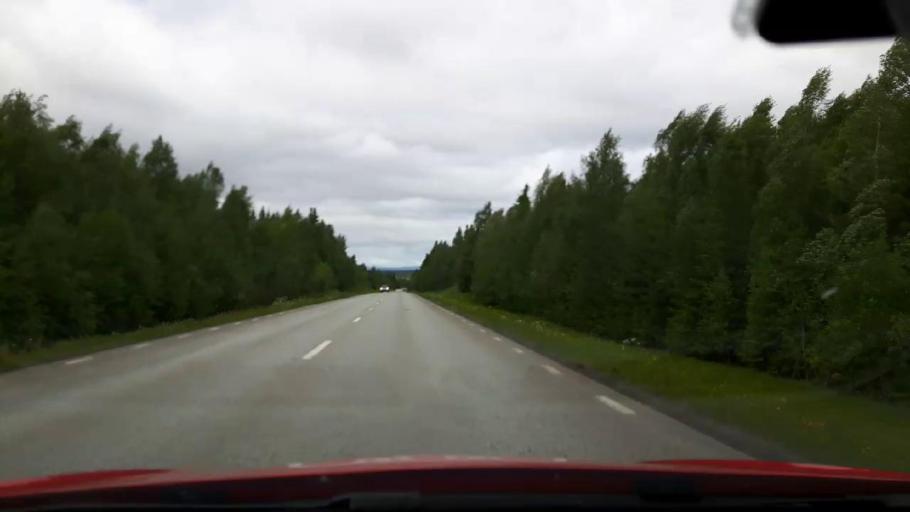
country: SE
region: Jaemtland
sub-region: Krokoms Kommun
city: Krokom
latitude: 63.3924
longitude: 14.5029
